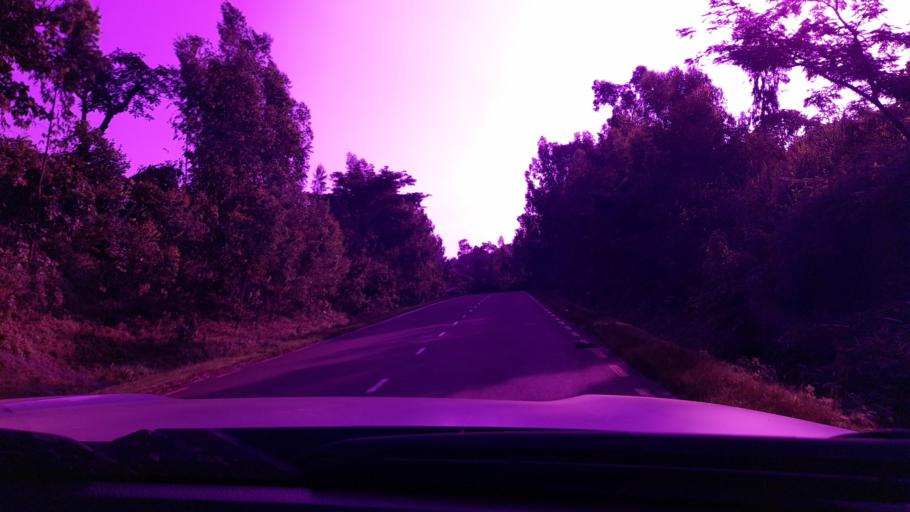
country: ET
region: Oromiya
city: Bedele
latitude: 8.1403
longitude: 36.4574
